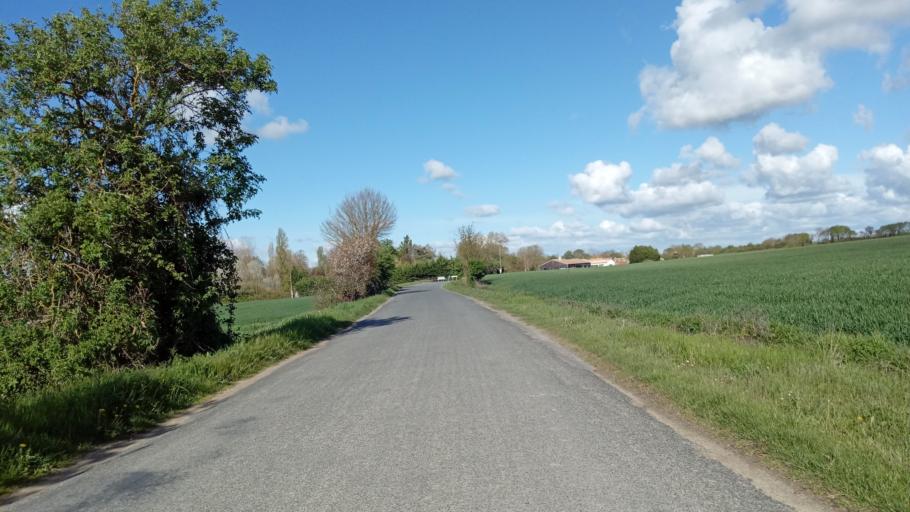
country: FR
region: Poitou-Charentes
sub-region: Departement de la Charente-Maritime
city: Verines
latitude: 46.1508
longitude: -0.9342
